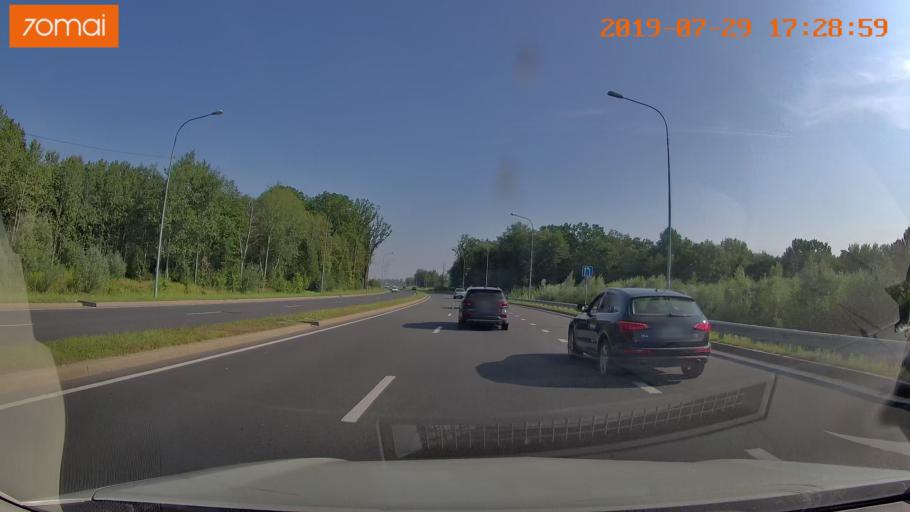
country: RU
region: Kaliningrad
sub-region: Gorod Kaliningrad
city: Kaliningrad
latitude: 54.7585
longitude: 20.4708
